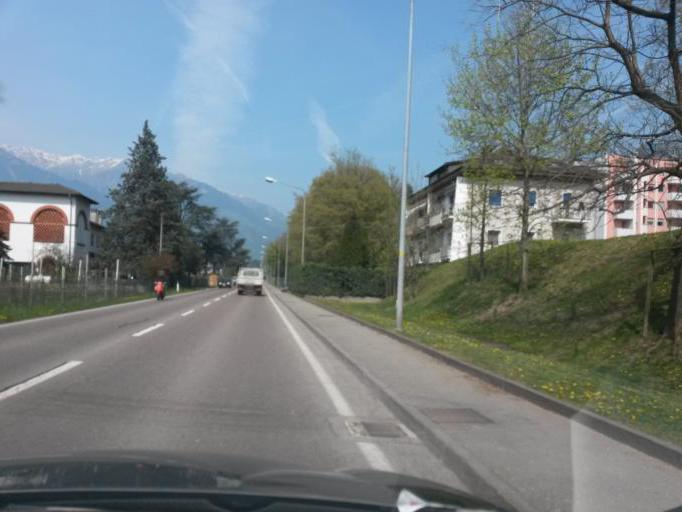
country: IT
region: Trentino-Alto Adige
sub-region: Bolzano
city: Sinigo
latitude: 46.6436
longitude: 11.1775
